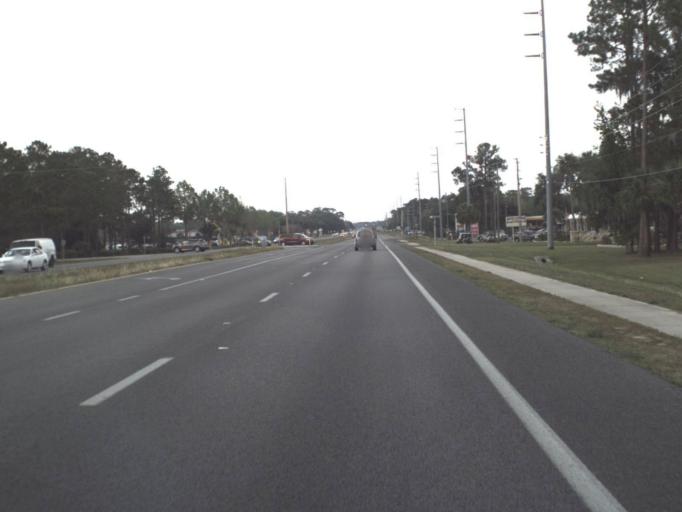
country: US
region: Florida
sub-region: Lake County
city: Eustis
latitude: 28.8712
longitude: -81.6880
